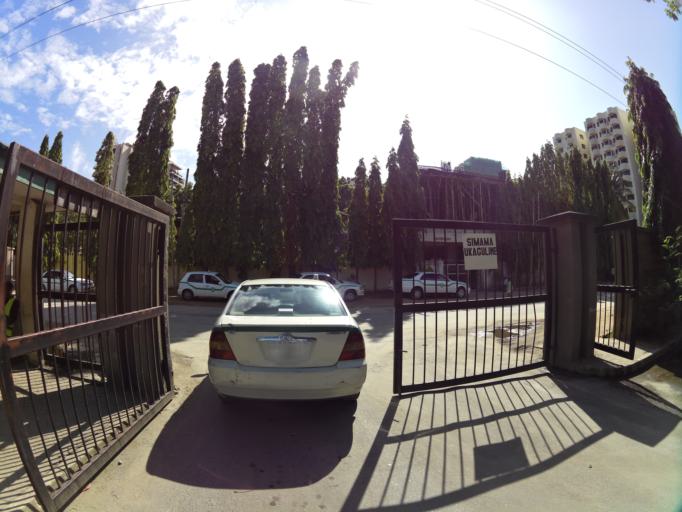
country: TZ
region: Dar es Salaam
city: Dar es Salaam
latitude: -6.8014
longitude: 39.2743
